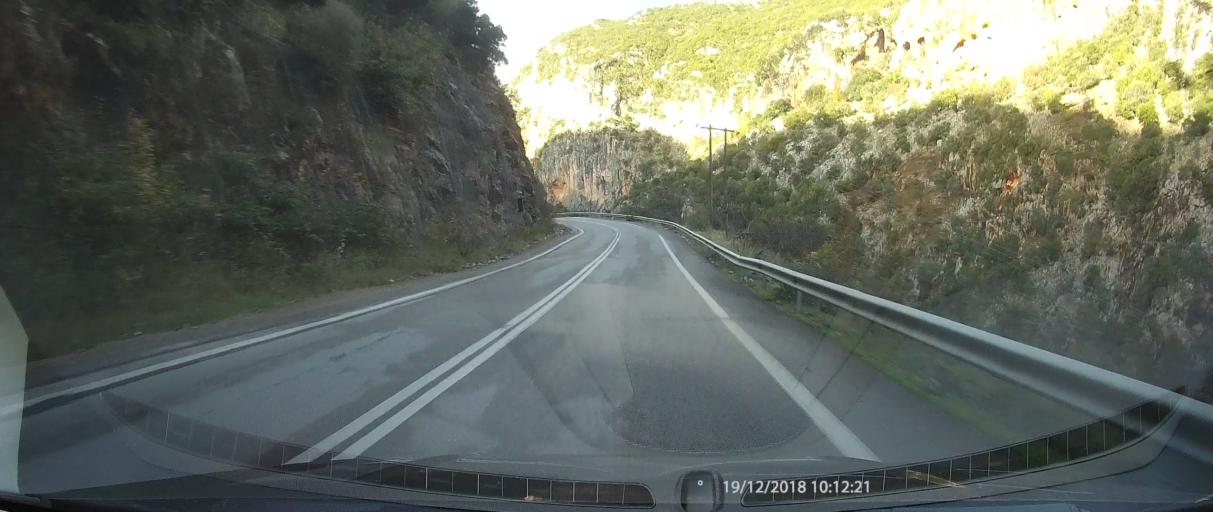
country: GR
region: Peloponnese
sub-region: Nomos Messinias
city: Kalamata
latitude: 37.0908
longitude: 22.1690
